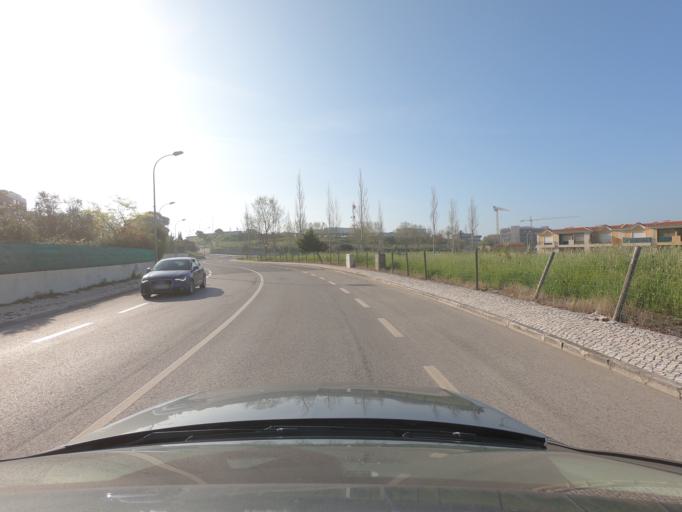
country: PT
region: Lisbon
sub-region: Oeiras
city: Carcavelos
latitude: 38.6822
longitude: -9.3243
